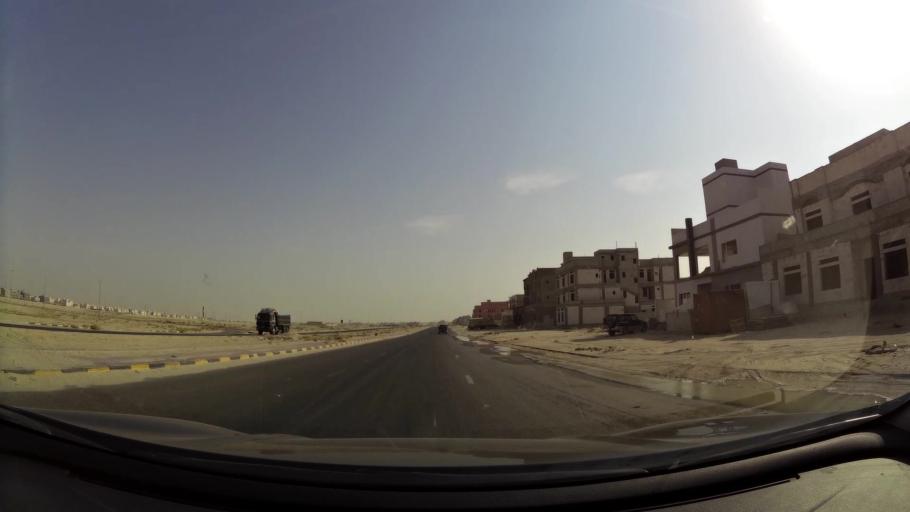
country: KW
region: Al Ahmadi
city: Al Wafrah
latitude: 28.7783
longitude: 48.0631
